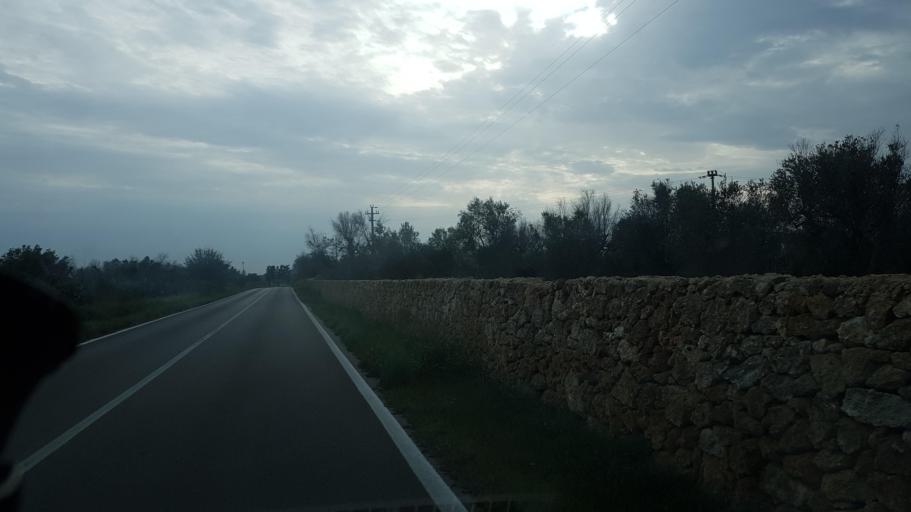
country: IT
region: Apulia
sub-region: Provincia di Lecce
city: Trepuzzi
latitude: 40.4304
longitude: 18.0756
